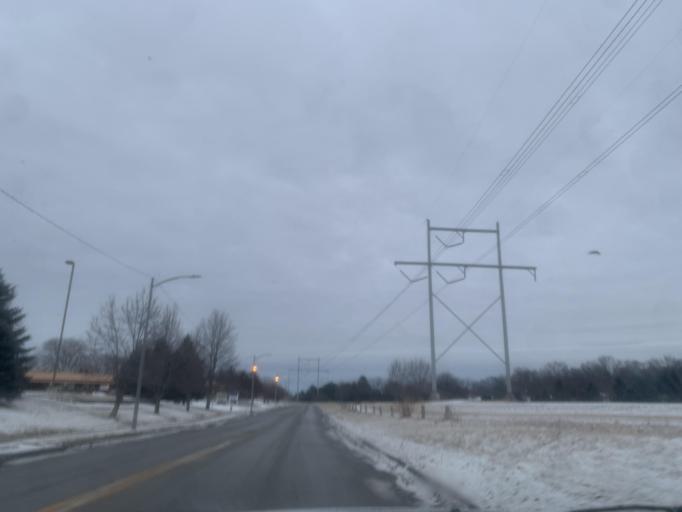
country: US
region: Nebraska
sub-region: Douglas County
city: Ralston
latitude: 41.2323
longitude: -96.0519
